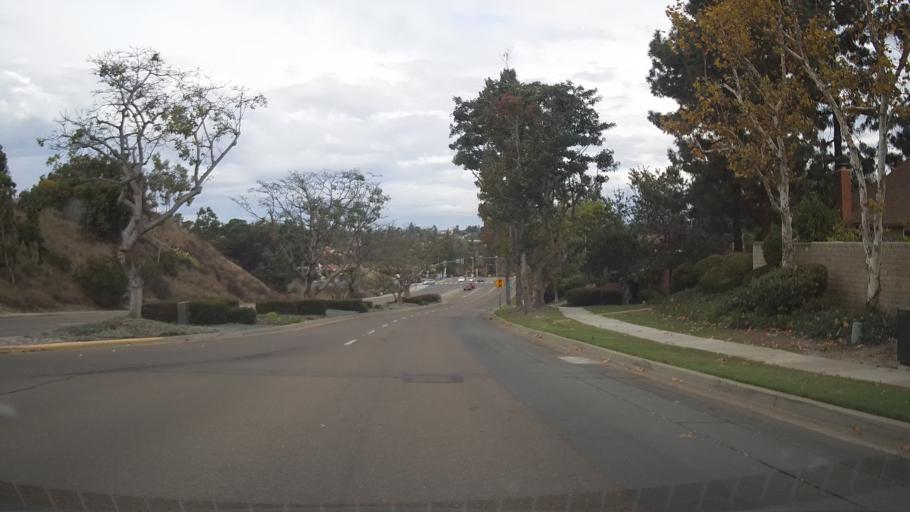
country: US
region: California
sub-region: San Diego County
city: La Mesa
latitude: 32.8273
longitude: -117.1038
